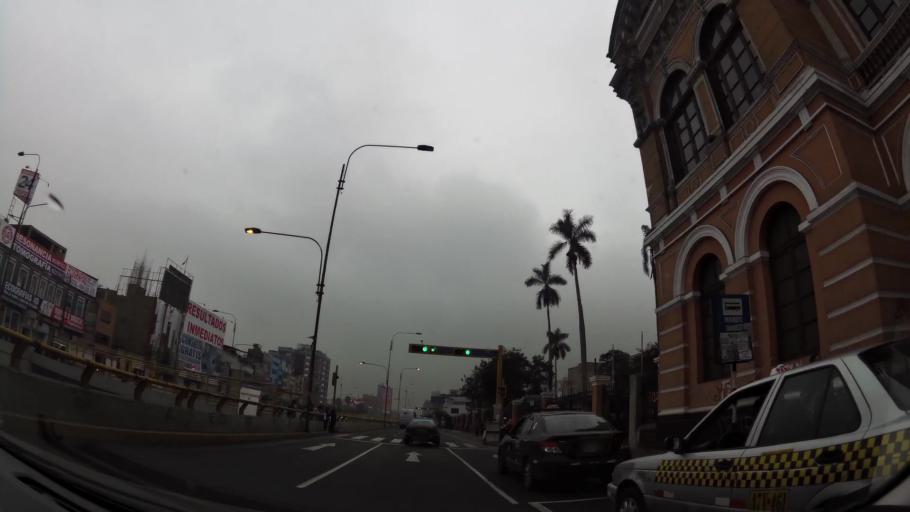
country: PE
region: Lima
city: Lima
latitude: -12.0581
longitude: -77.0231
